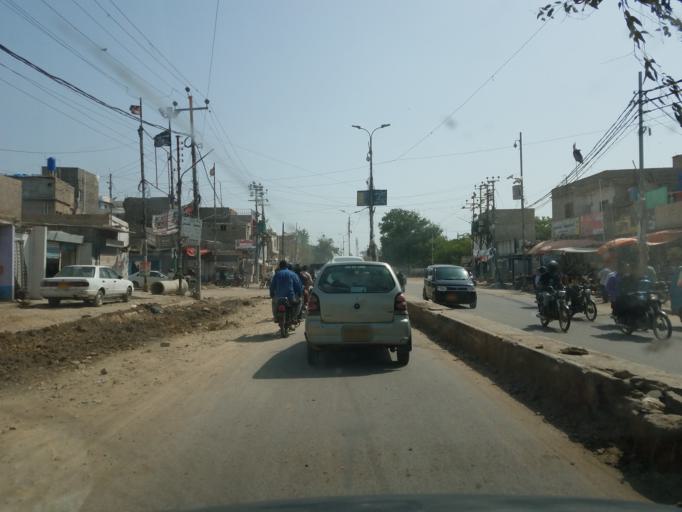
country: PK
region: Sindh
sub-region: Karachi District
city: Karachi
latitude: 24.8890
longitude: 67.0424
